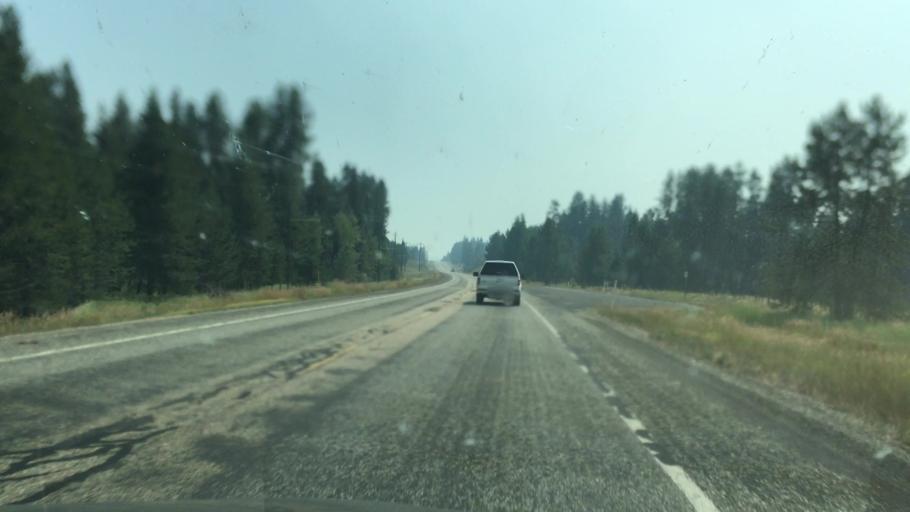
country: US
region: Idaho
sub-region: Valley County
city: Cascade
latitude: 44.3880
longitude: -116.0110
